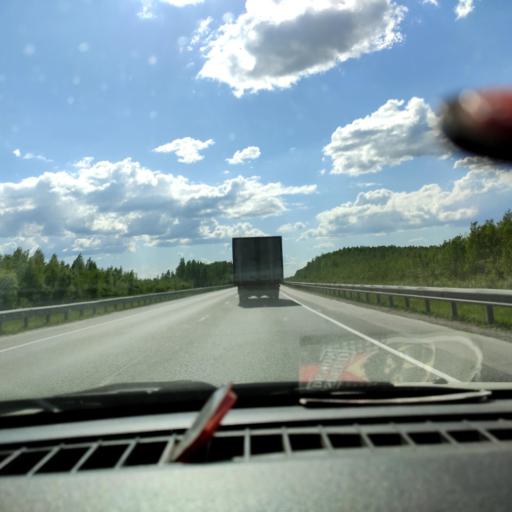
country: RU
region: Perm
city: Krasnokamsk
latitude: 58.1060
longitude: 55.7795
